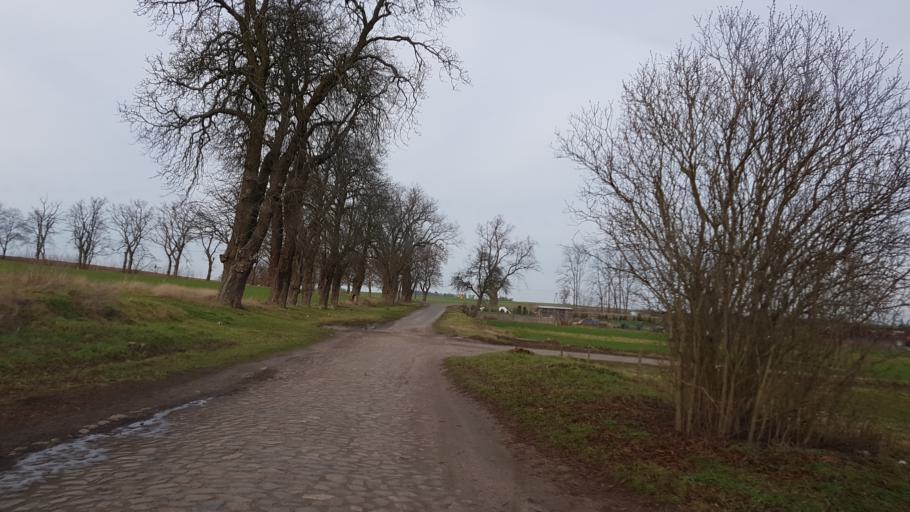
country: PL
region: Lubusz
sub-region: Powiat strzelecko-drezdenecki
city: Strzelce Krajenskie
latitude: 52.9299
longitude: 15.4177
